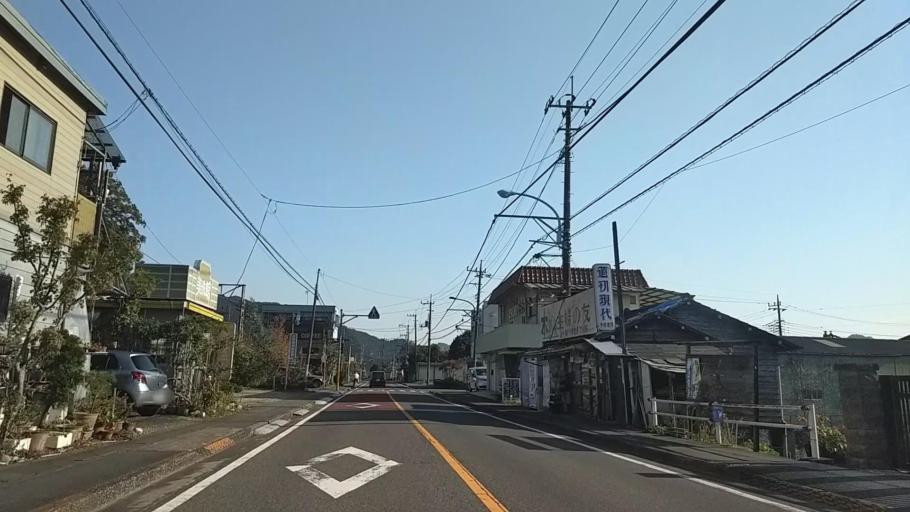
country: JP
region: Tokyo
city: Ome
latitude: 35.8036
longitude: 139.2162
